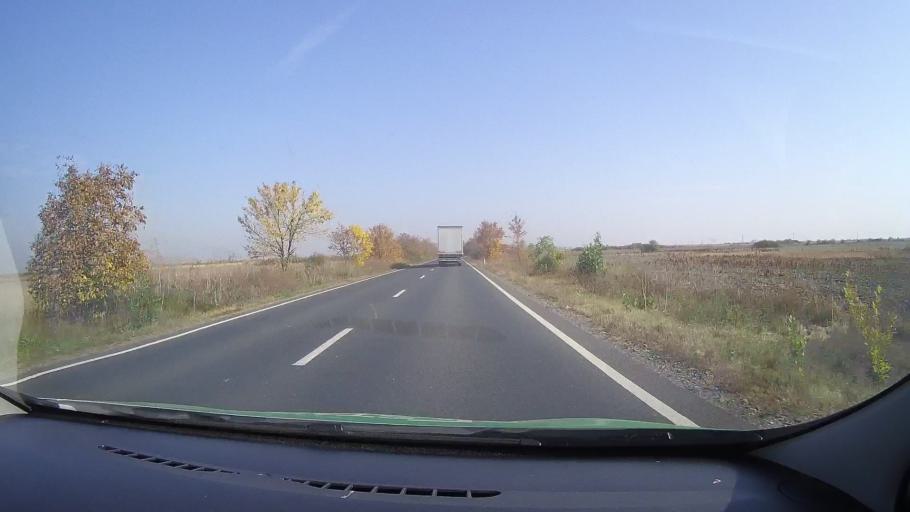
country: RO
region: Bihor
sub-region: Comuna Ciumeghiu
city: Ciumeghiu
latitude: 46.7685
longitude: 21.6132
